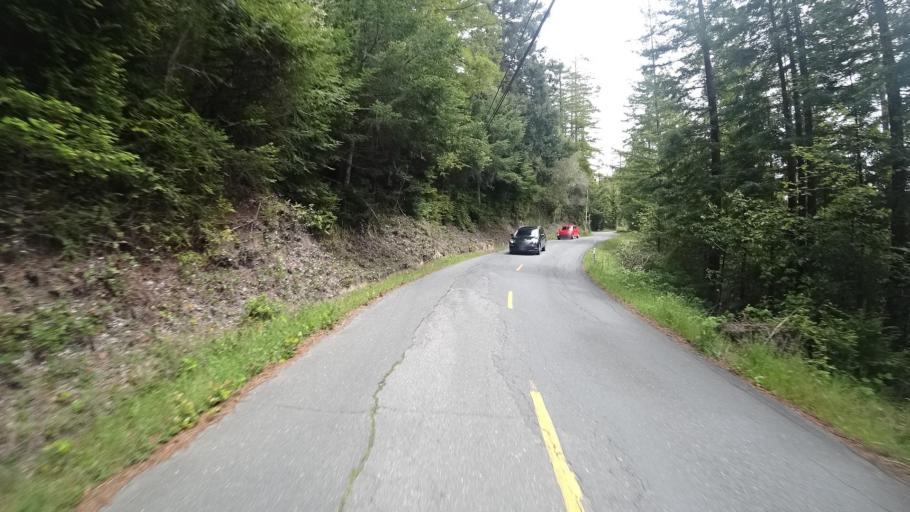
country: US
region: California
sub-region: Humboldt County
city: Bayside
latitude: 40.7870
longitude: -124.0664
